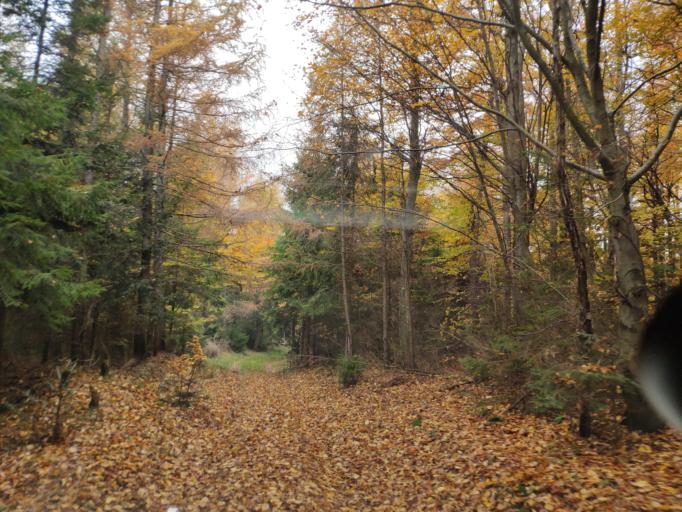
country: SK
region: Kosicky
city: Medzev
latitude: 48.7453
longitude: 20.9880
